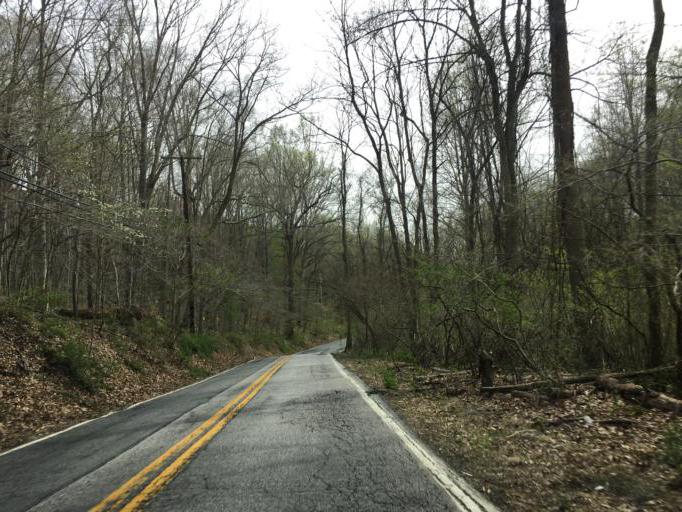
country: US
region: Maryland
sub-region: Baltimore County
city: Hunt Valley
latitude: 39.5253
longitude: -76.6145
